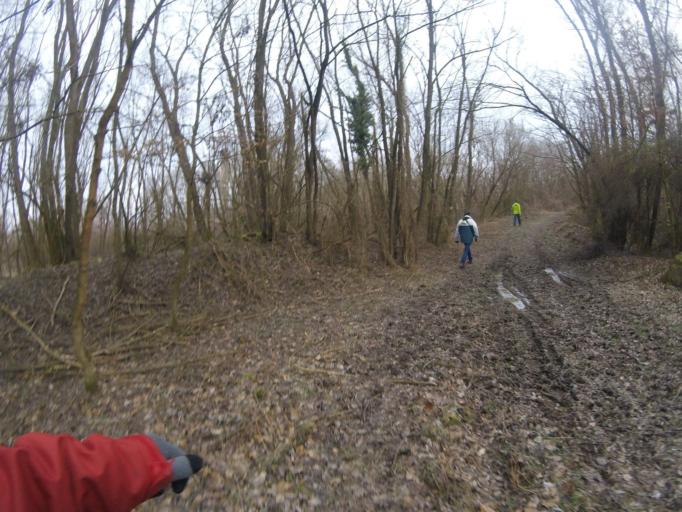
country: HU
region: Baranya
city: Mecseknadasd
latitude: 46.1484
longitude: 18.5151
